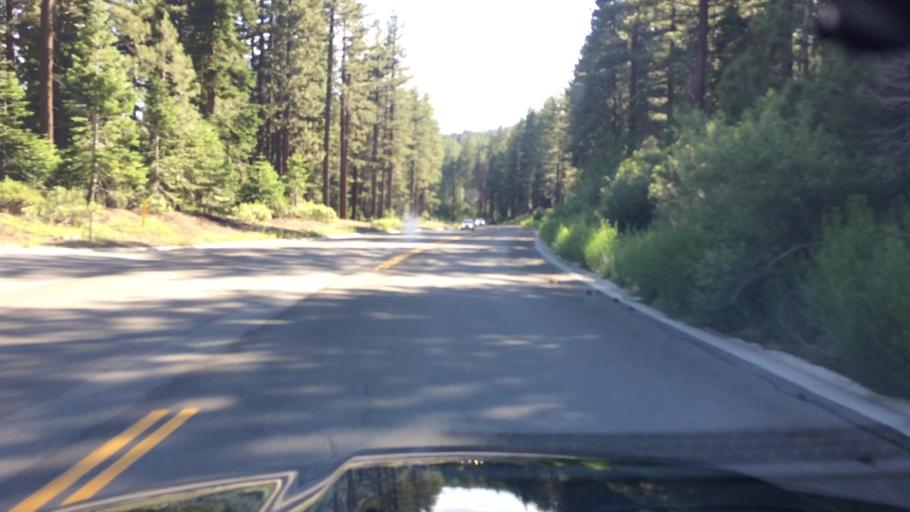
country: US
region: Nevada
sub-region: Washoe County
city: Incline Village
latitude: 39.2711
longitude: -119.9507
